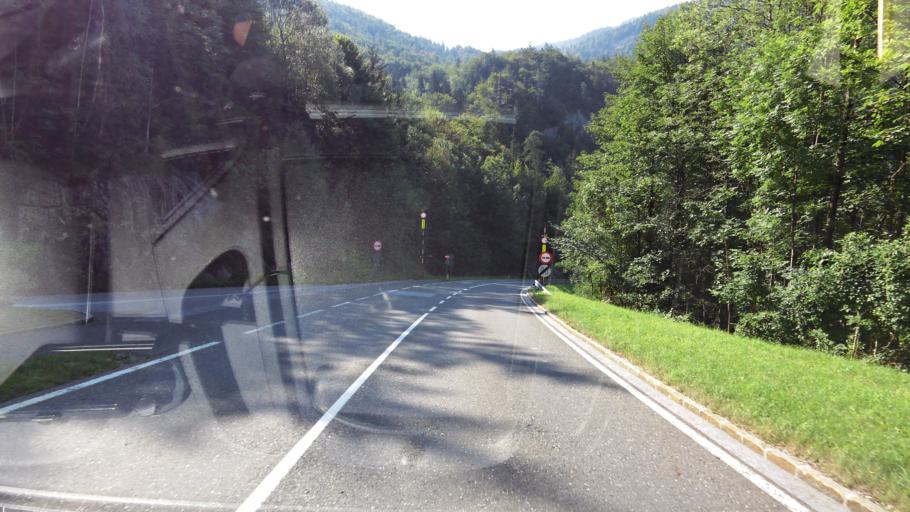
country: AT
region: Salzburg
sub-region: Politischer Bezirk Hallein
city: Scheffau am Tennengebirge
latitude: 47.5749
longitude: 13.1949
